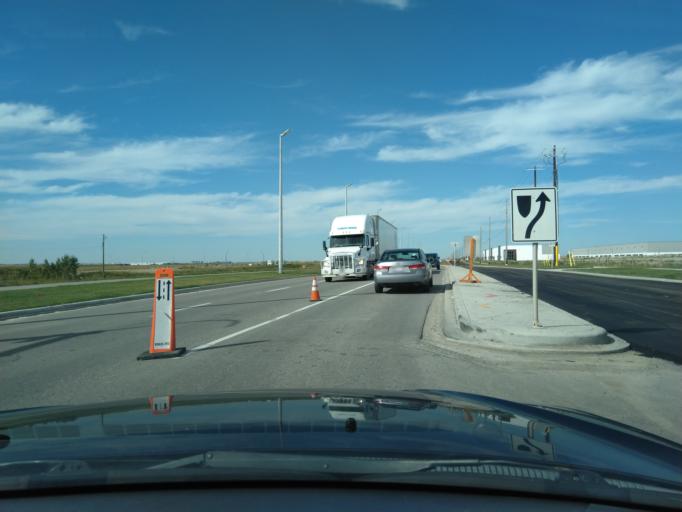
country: CA
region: Alberta
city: Calgary
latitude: 51.1254
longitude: -113.9817
